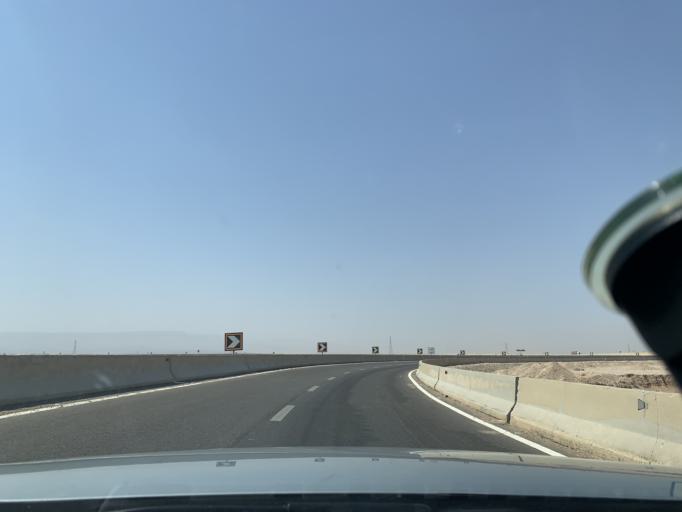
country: EG
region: As Suways
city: Ain Sukhna
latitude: 29.1064
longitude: 32.5303
